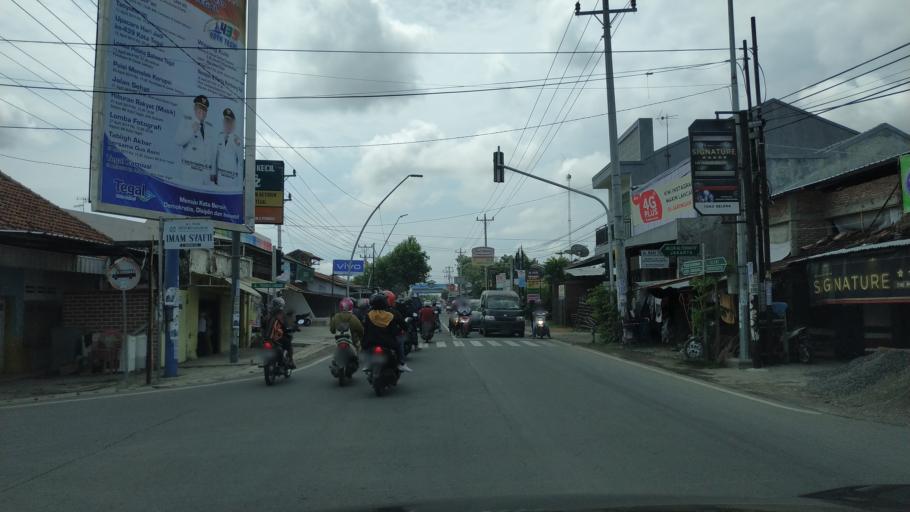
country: ID
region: Central Java
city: Tegal
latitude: -6.8974
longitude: 109.1258
